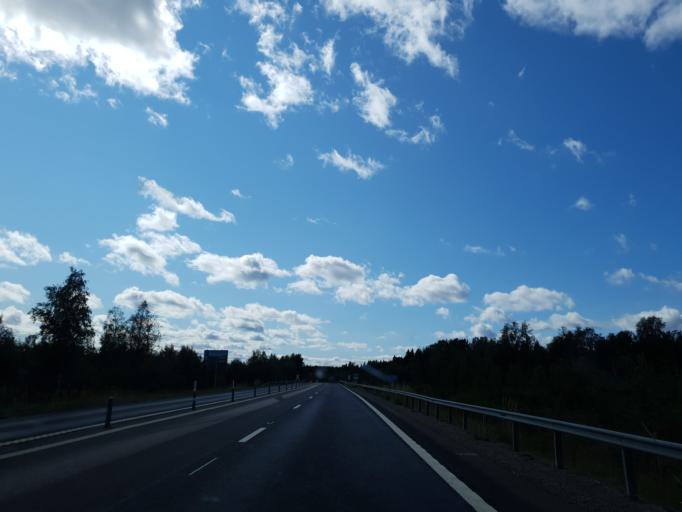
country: SE
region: Vaesterbotten
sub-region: Nordmalings Kommun
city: Nordmaling
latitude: 63.5698
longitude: 19.4365
